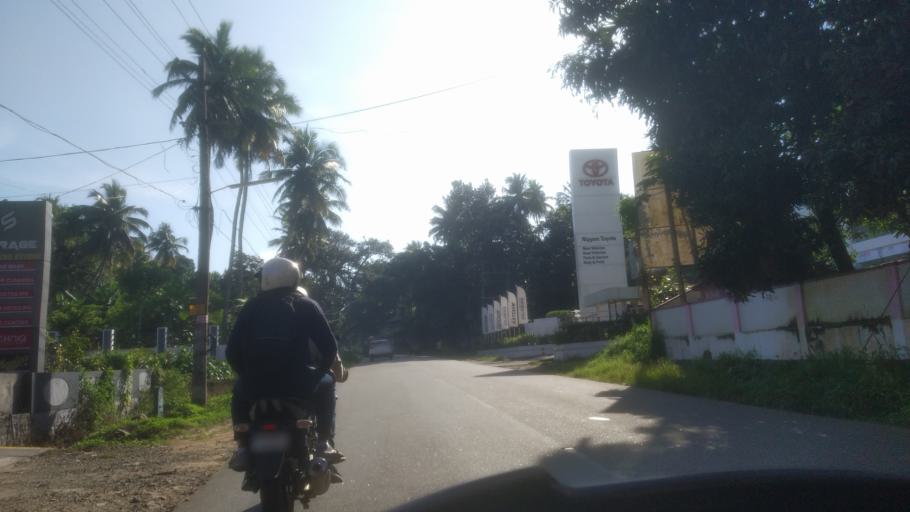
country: IN
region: Kerala
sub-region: Ernakulam
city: Muvattupuzha
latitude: 9.9786
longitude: 76.5351
